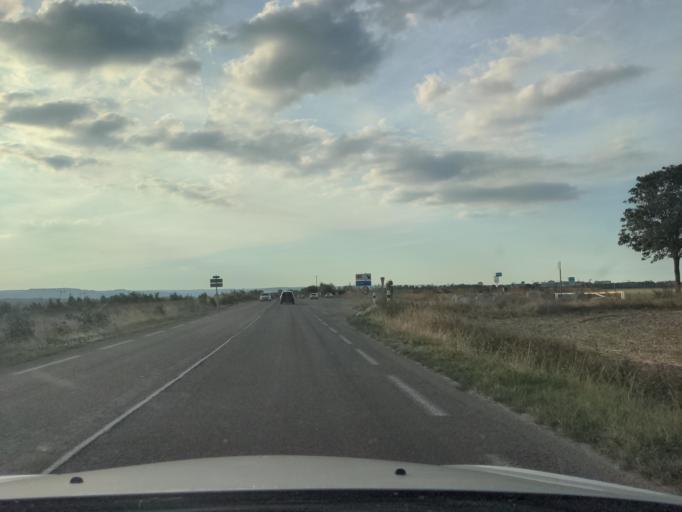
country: FR
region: Bourgogne
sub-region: Departement de la Cote-d'Or
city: Sennecey-les-Dijon
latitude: 47.2950
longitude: 5.0854
